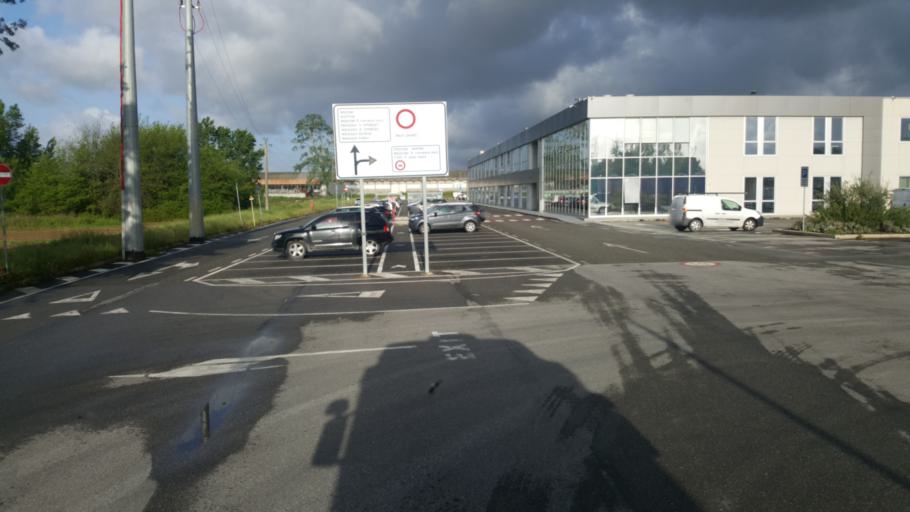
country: IT
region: Tuscany
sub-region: Provincia di Lucca
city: Porcari
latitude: 43.8530
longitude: 10.6033
